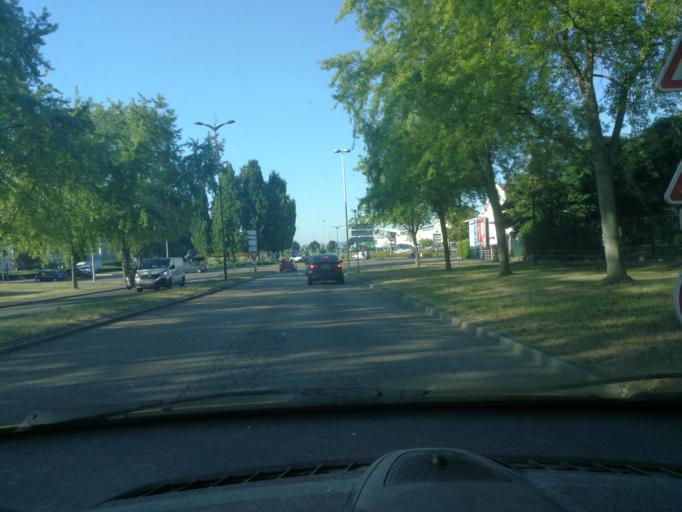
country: FR
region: Lorraine
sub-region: Departement de la Moselle
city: Terville
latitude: 49.3575
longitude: 6.1439
